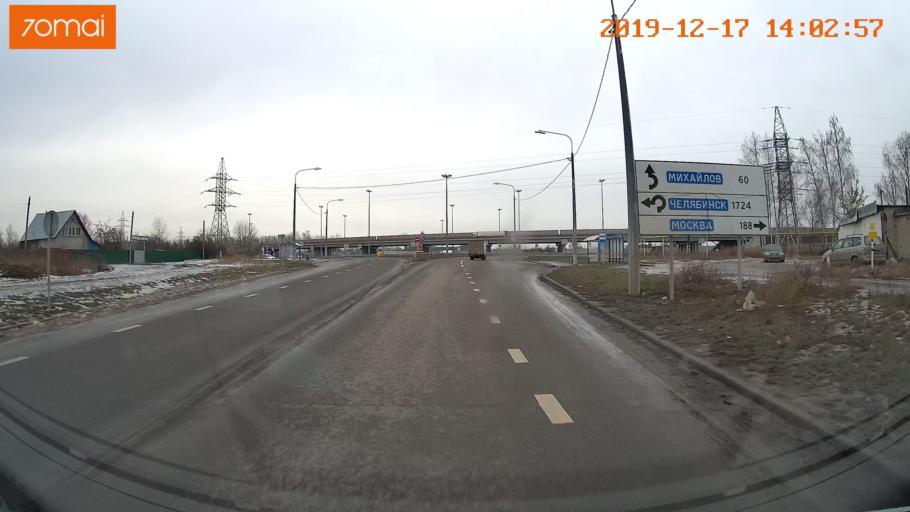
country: RU
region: Rjazan
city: Ryazan'
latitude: 54.6112
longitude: 39.6421
